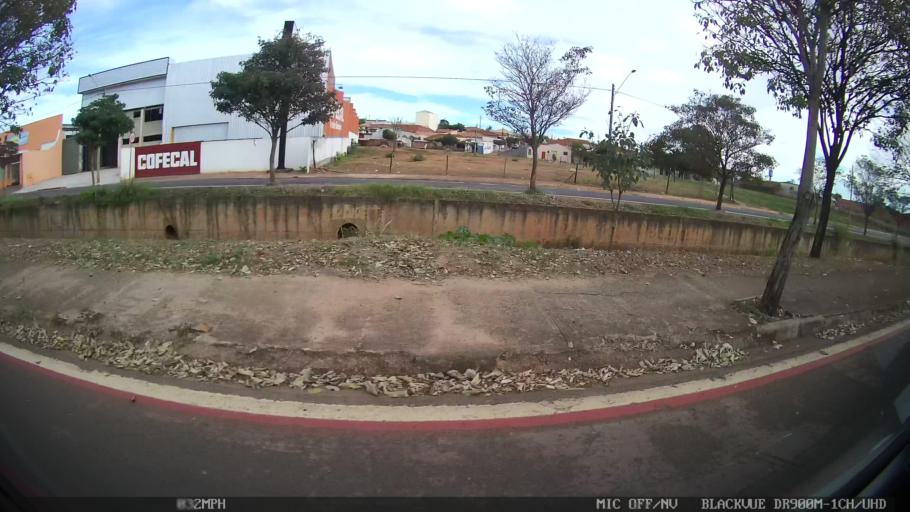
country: BR
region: Sao Paulo
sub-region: Catanduva
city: Catanduva
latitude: -21.1276
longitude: -48.9838
